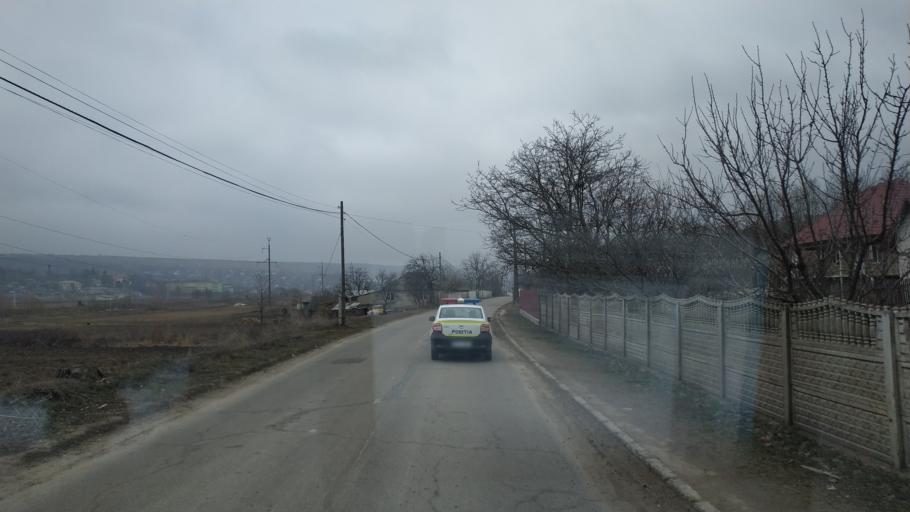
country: MD
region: Hincesti
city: Hincesti
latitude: 46.9790
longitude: 28.4581
